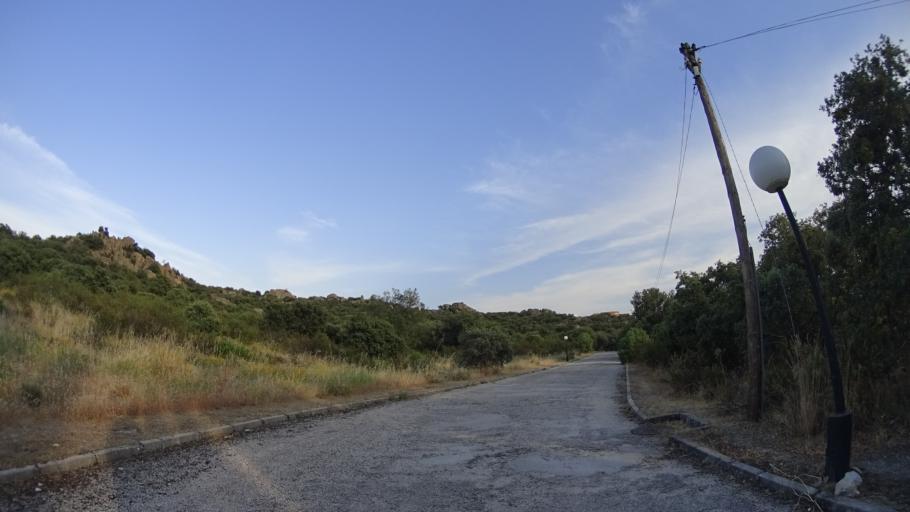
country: ES
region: Madrid
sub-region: Provincia de Madrid
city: Torrelodones
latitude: 40.5935
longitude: -3.9457
